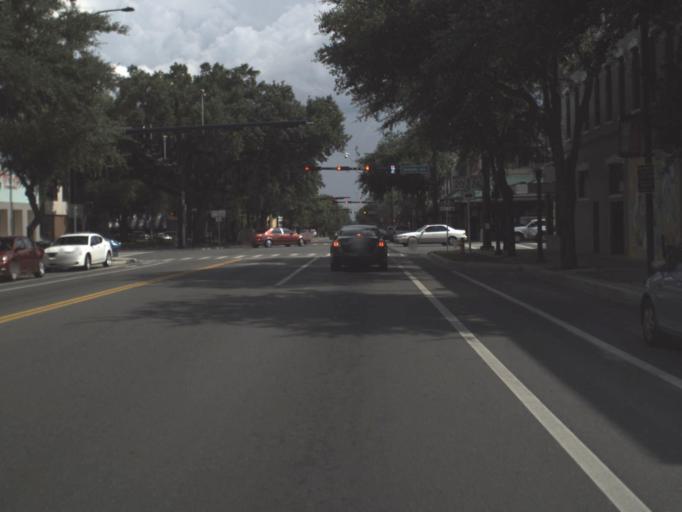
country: US
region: Florida
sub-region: Alachua County
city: Gainesville
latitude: 29.6526
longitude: -82.3251
